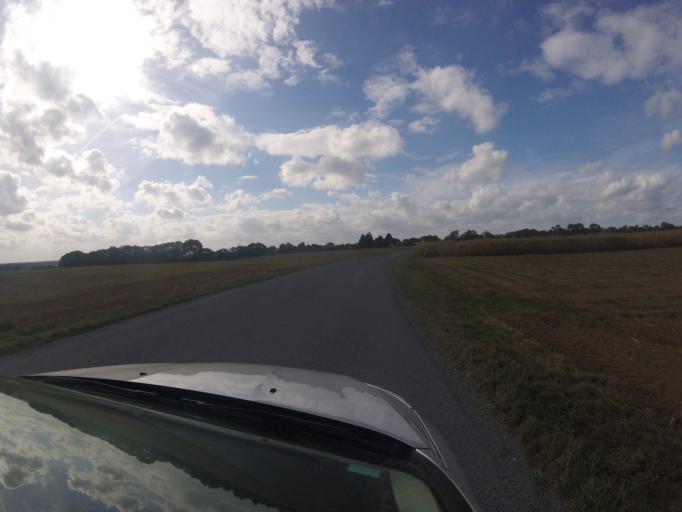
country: FR
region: Lower Normandy
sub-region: Departement du Calvados
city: Saint-Vigor-le-Grand
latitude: 49.3336
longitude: -0.6840
